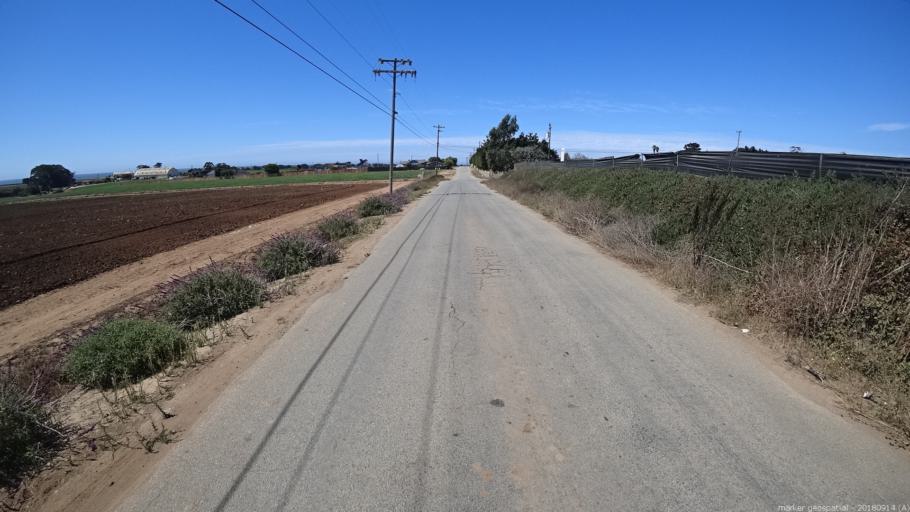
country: US
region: California
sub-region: Monterey County
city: Las Lomas
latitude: 36.8561
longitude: -121.7957
